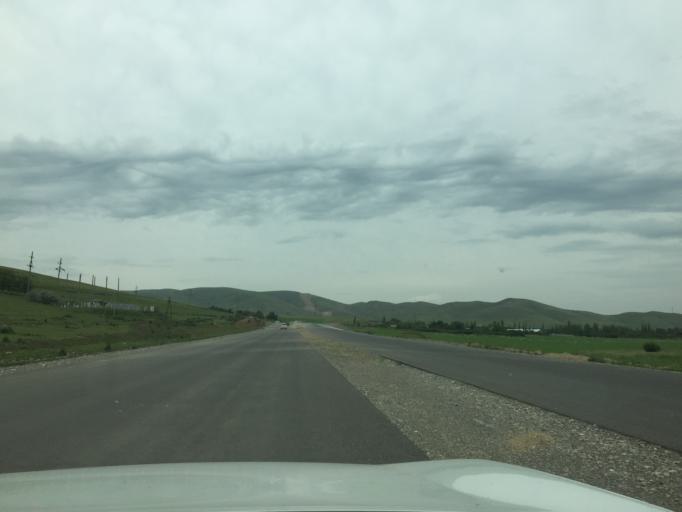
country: KZ
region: Ongtustik Qazaqstan
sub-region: Tulkibas Audany
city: Zhabagly
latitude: 42.5116
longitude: 70.5271
